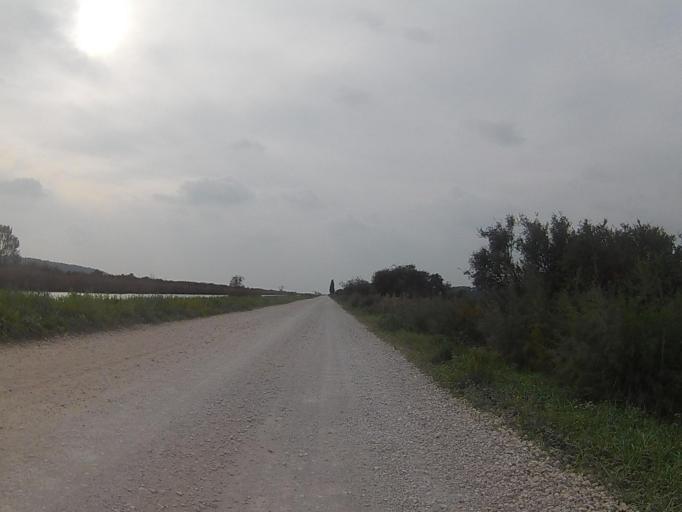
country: HR
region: Istarska
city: Novigrad
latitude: 45.3225
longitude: 13.6081
